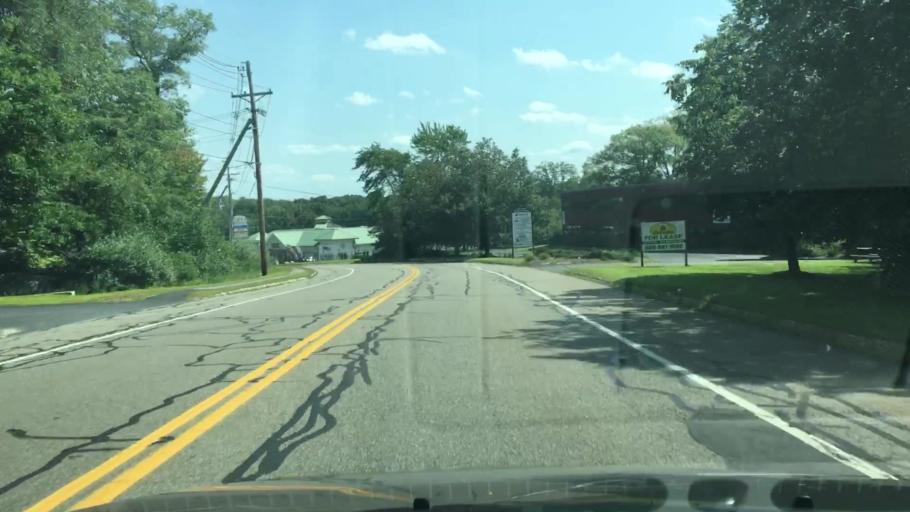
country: US
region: Massachusetts
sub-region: Worcester County
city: Milford
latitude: 42.1552
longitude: -71.4925
